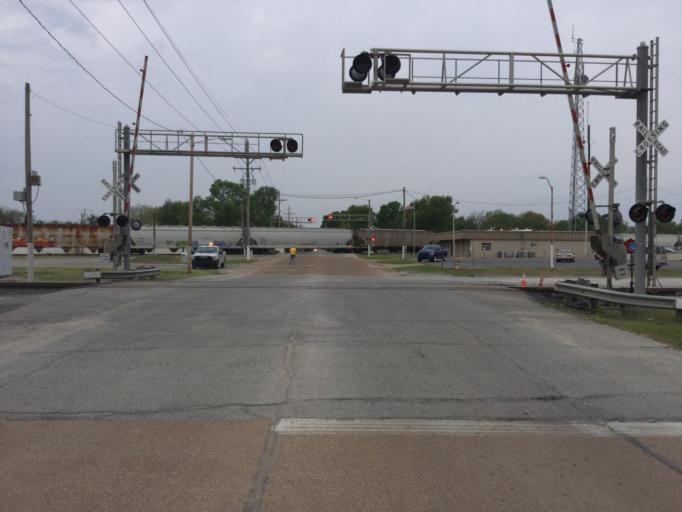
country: US
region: Kansas
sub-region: Labette County
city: Parsons
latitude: 37.3425
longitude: -95.2662
